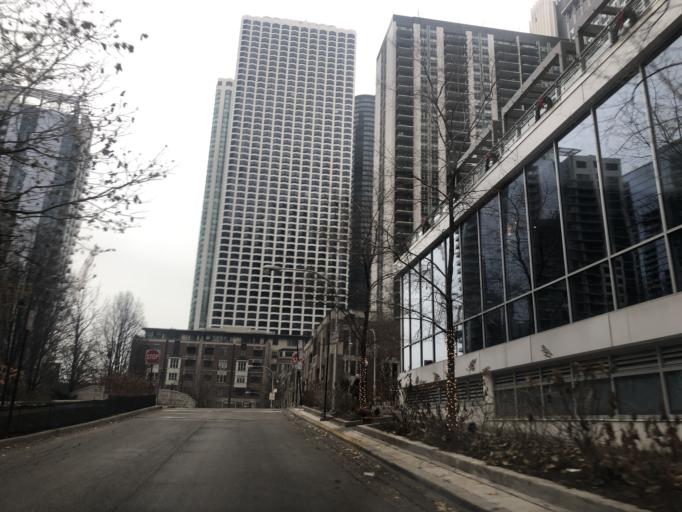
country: US
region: Illinois
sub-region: Cook County
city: Chicago
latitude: 41.8855
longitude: -87.6178
